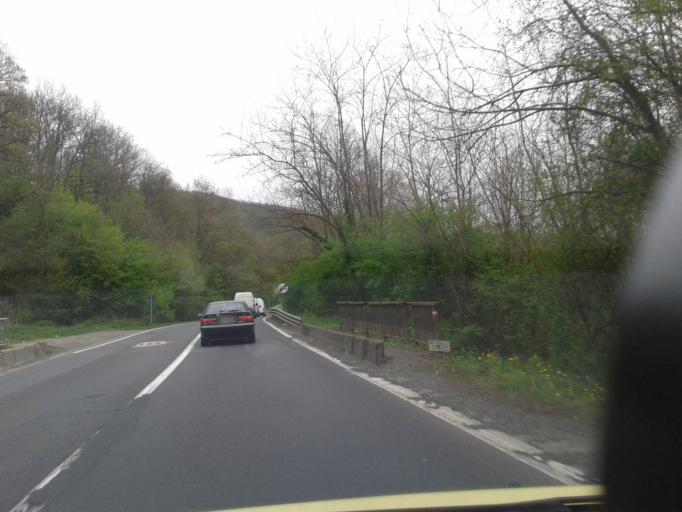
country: RO
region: Arad
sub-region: Comuna Bata
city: Bata
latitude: 46.0747
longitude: 22.0330
